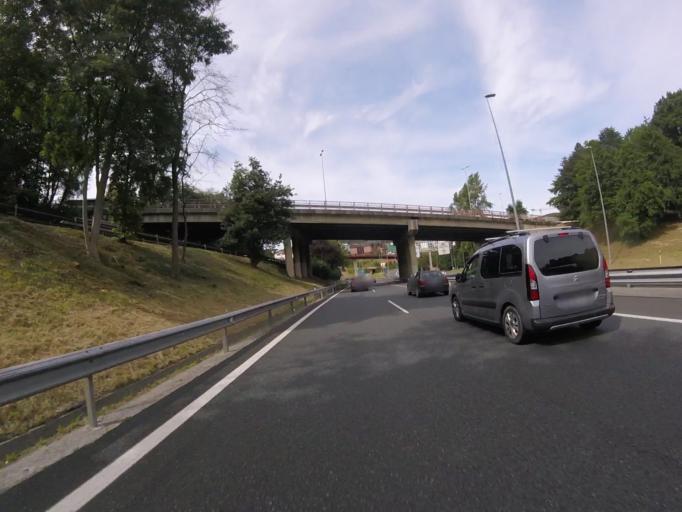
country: ES
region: Basque Country
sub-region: Provincia de Guipuzcoa
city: Pasaia
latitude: 43.3130
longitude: -1.9437
